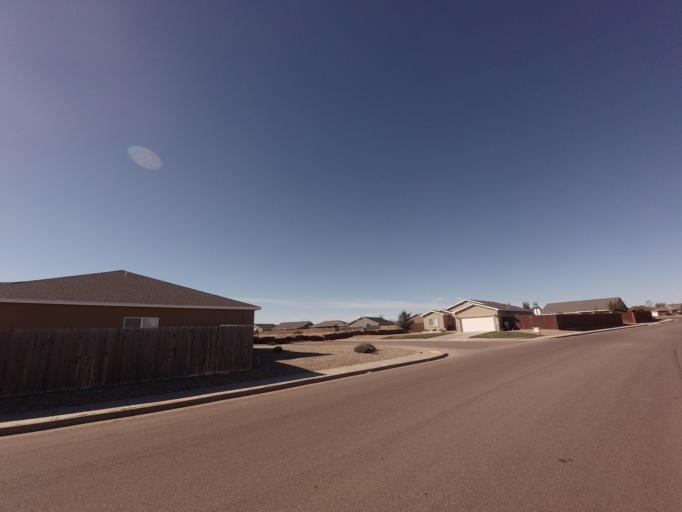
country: US
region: New Mexico
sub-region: Curry County
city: Clovis
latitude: 34.4148
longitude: -103.1641
